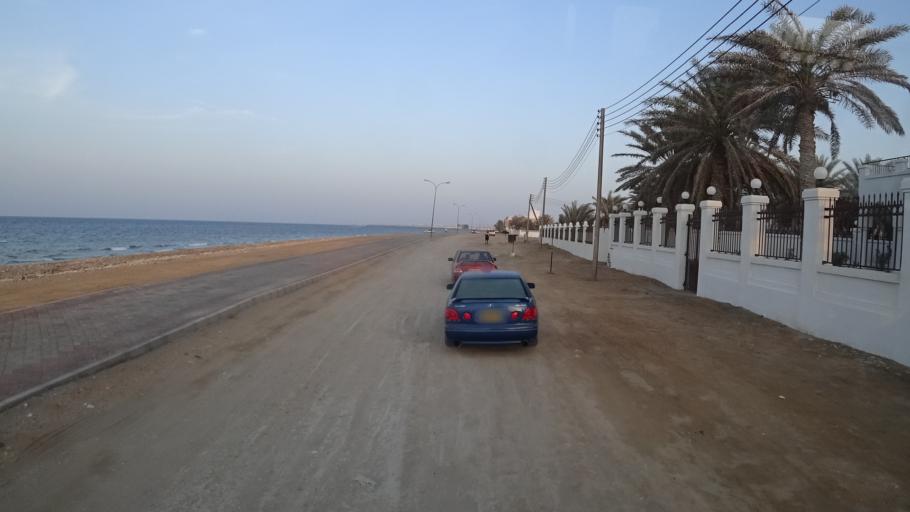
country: OM
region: Ash Sharqiyah
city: Sur
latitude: 22.5917
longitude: 59.5025
